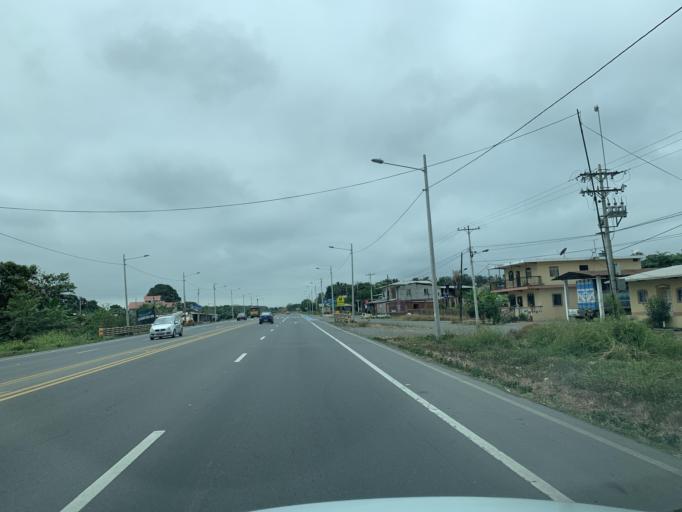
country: EC
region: Guayas
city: Coronel Marcelino Mariduena
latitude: -2.3158
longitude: -79.4702
